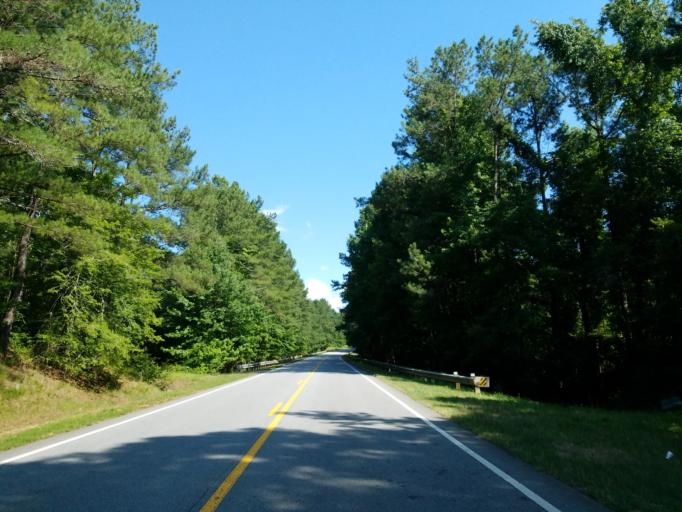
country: US
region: Georgia
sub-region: Crawford County
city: Roberta
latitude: 32.8406
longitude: -84.0666
